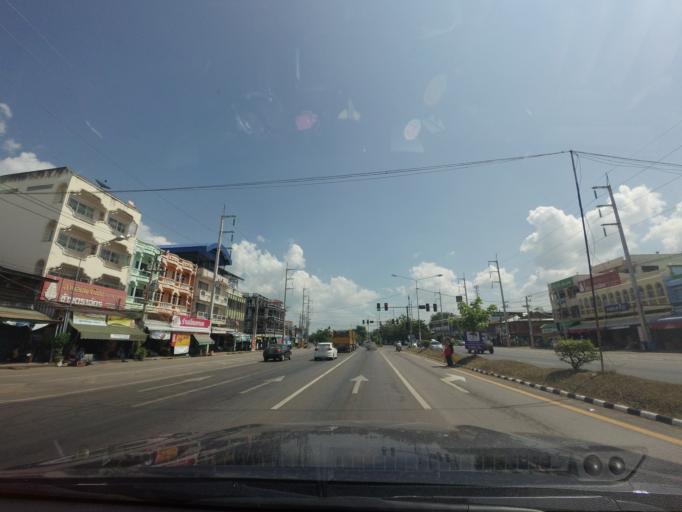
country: TH
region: Phetchabun
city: Nong Phai
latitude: 16.0815
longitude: 101.0579
